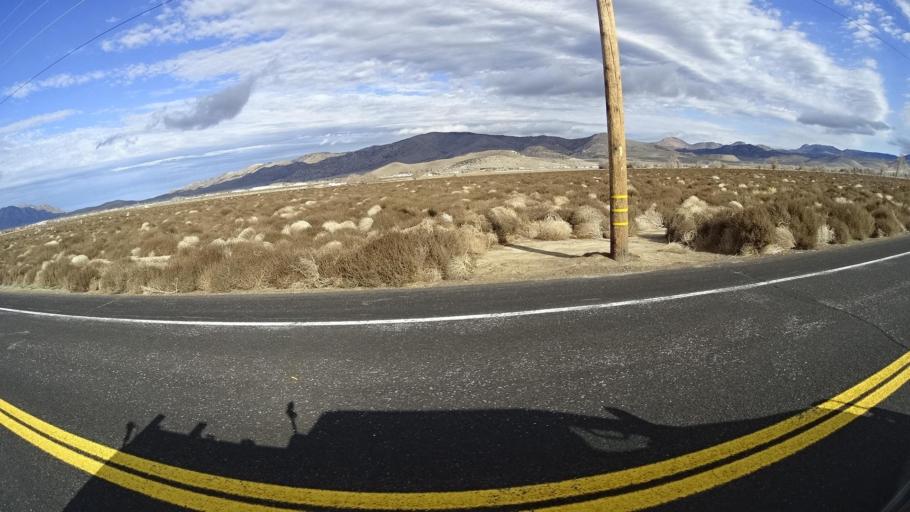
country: US
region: California
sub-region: Kern County
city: Tehachapi
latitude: 35.1097
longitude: -118.4133
